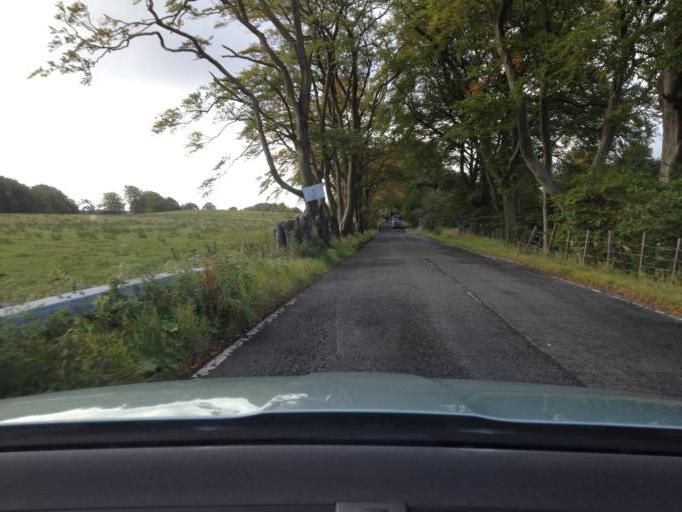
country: GB
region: Scotland
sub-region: West Lothian
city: West Calder
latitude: 55.8359
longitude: -3.5344
